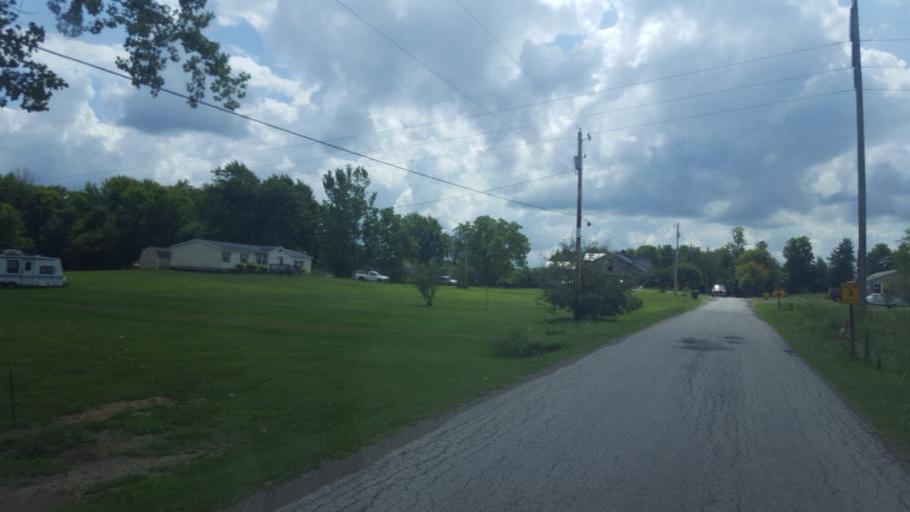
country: US
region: Ohio
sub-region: Knox County
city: Centerburg
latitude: 40.4339
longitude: -82.7473
